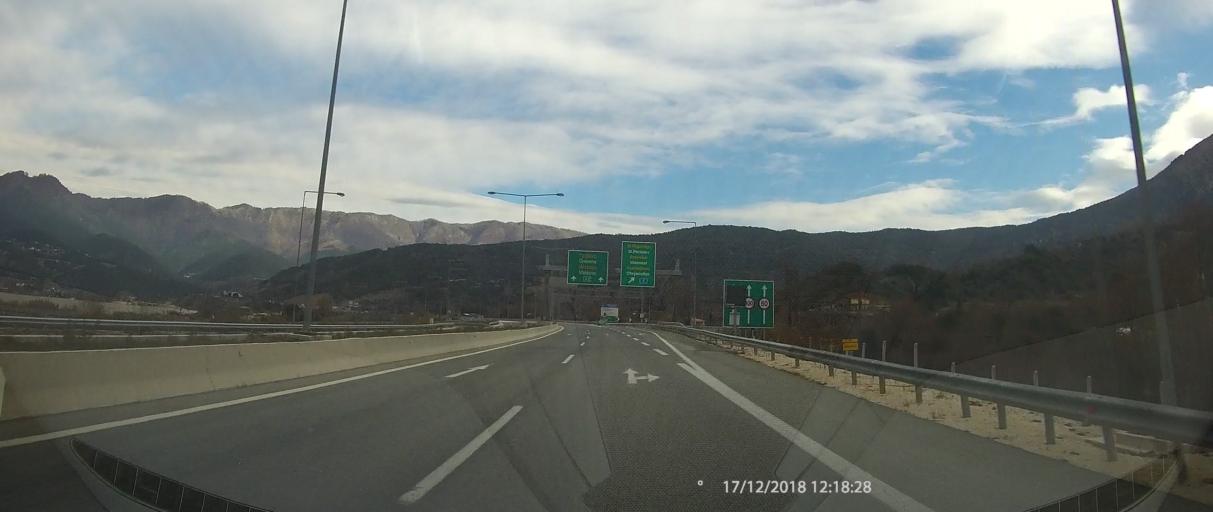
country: GR
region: Epirus
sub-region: Nomos Ioanninon
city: Metsovo
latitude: 39.7530
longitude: 21.0850
